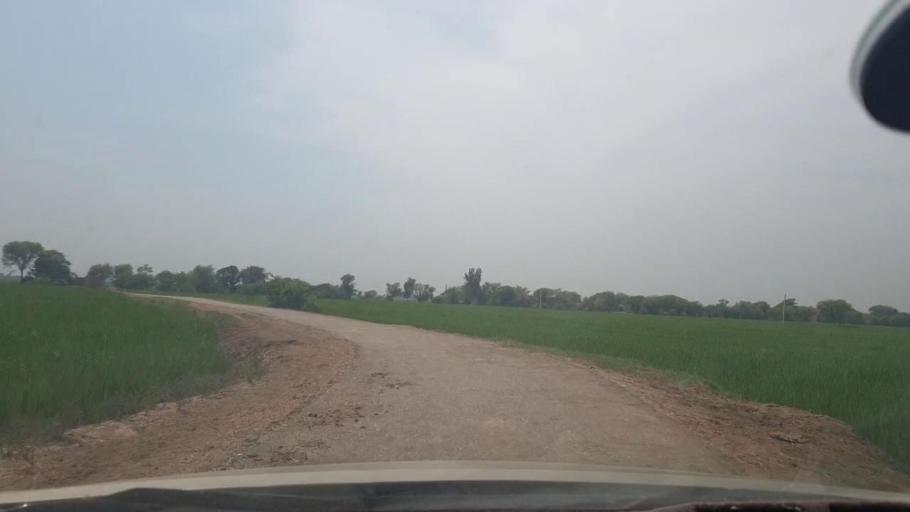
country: PK
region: Sindh
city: Jacobabad
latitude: 28.2400
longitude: 68.4195
